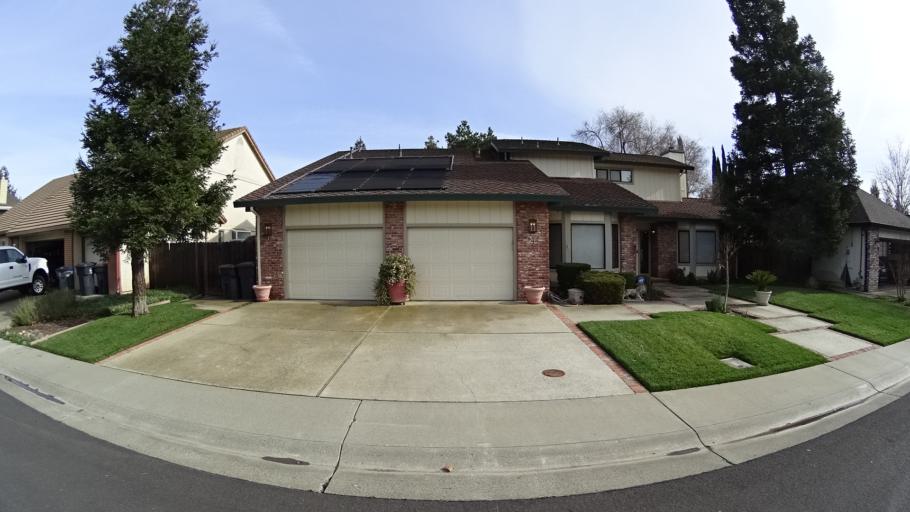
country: US
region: California
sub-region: Yolo County
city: Davis
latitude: 38.5500
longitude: -121.6817
